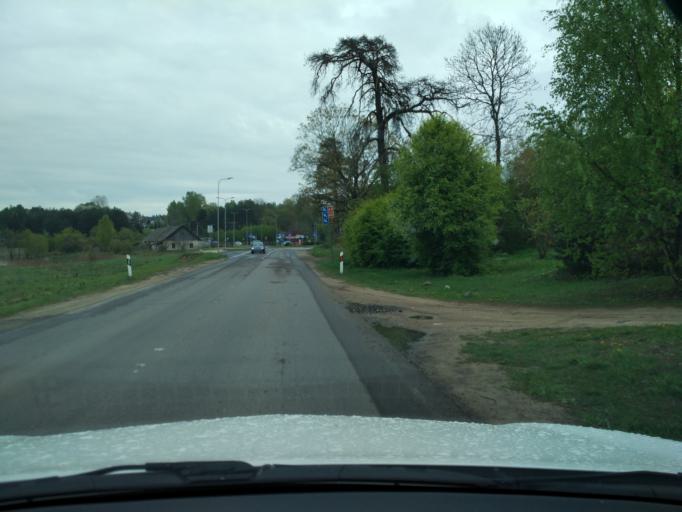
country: LT
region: Vilnius County
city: Rasos
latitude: 54.7376
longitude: 25.4015
